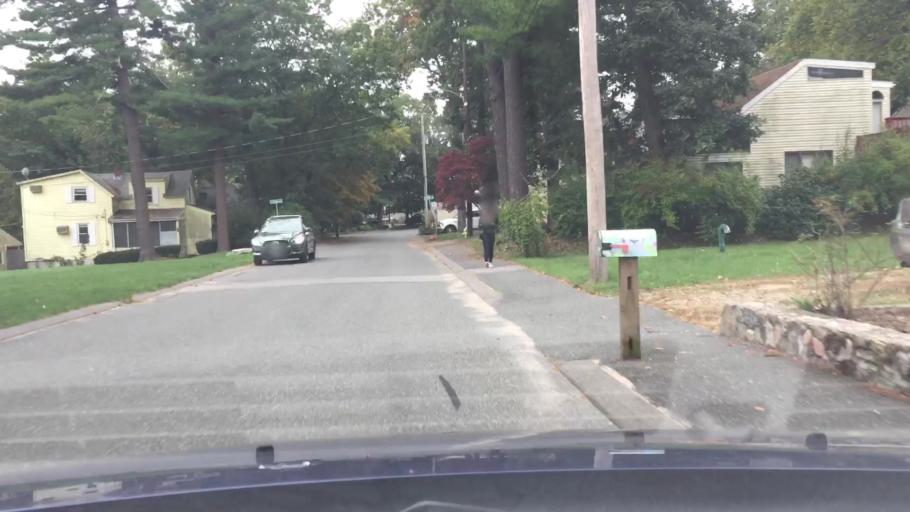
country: US
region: Massachusetts
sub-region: Essex County
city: Middleton
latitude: 42.5804
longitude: -71.0056
